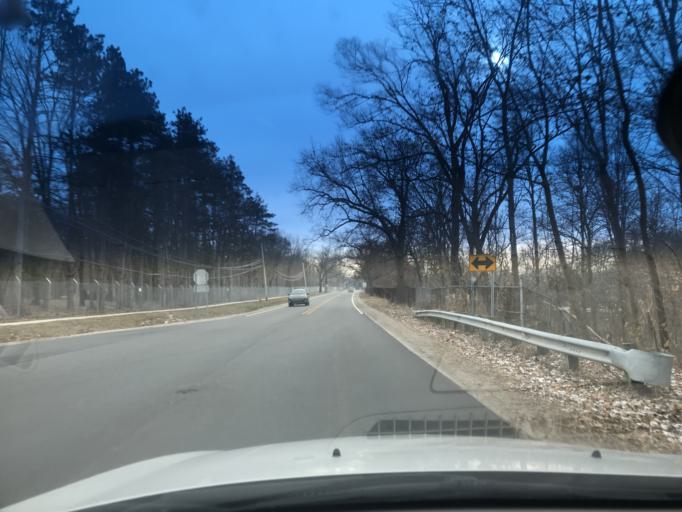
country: US
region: Michigan
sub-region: Macomb County
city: Shelby
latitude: 42.6581
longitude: -83.0533
